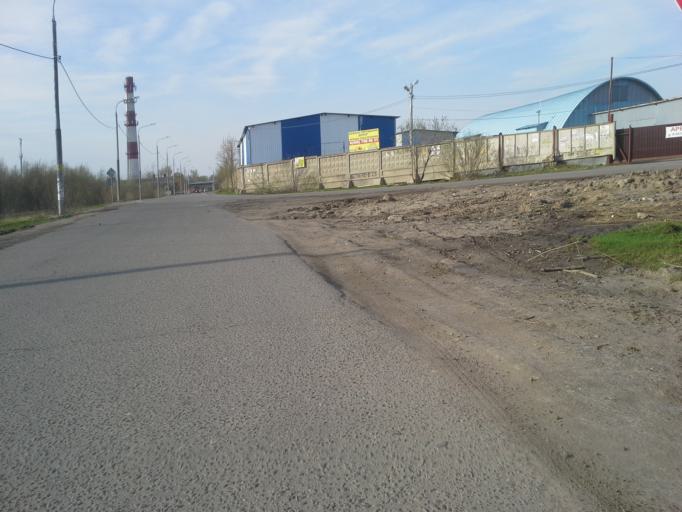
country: RU
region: Moskovskaya
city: Kommunarka
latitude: 55.5166
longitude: 37.4525
